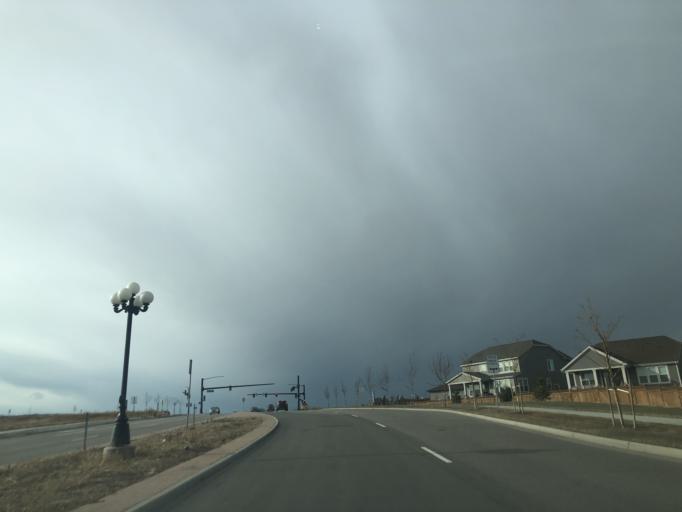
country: US
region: Colorado
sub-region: Douglas County
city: Stonegate
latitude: 39.5560
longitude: -104.8051
